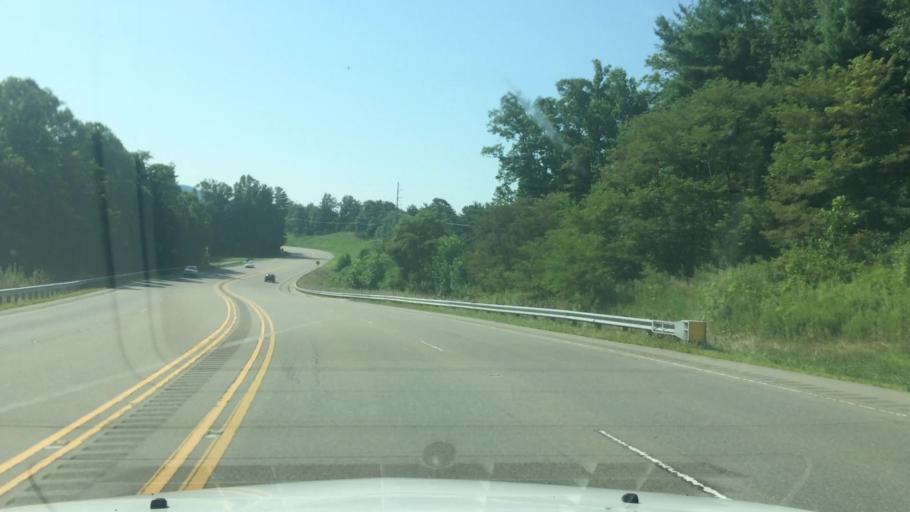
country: US
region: North Carolina
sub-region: Watauga County
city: Blowing Rock
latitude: 36.0675
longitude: -81.6151
